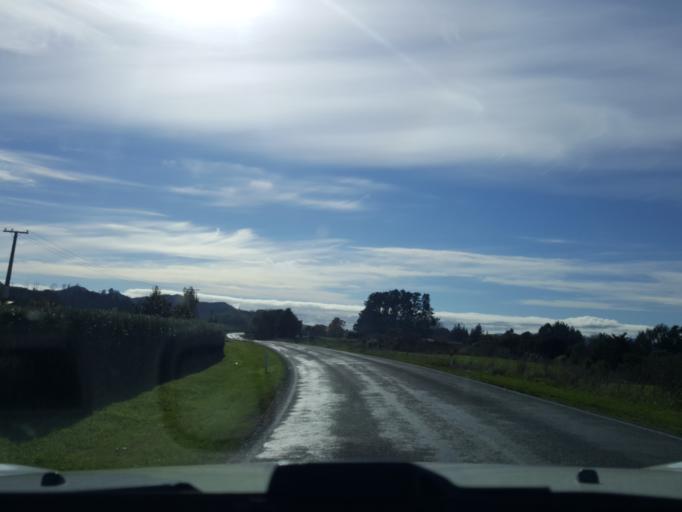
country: NZ
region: Waikato
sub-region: Waikato District
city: Ngaruawahia
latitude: -37.6087
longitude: 175.1972
